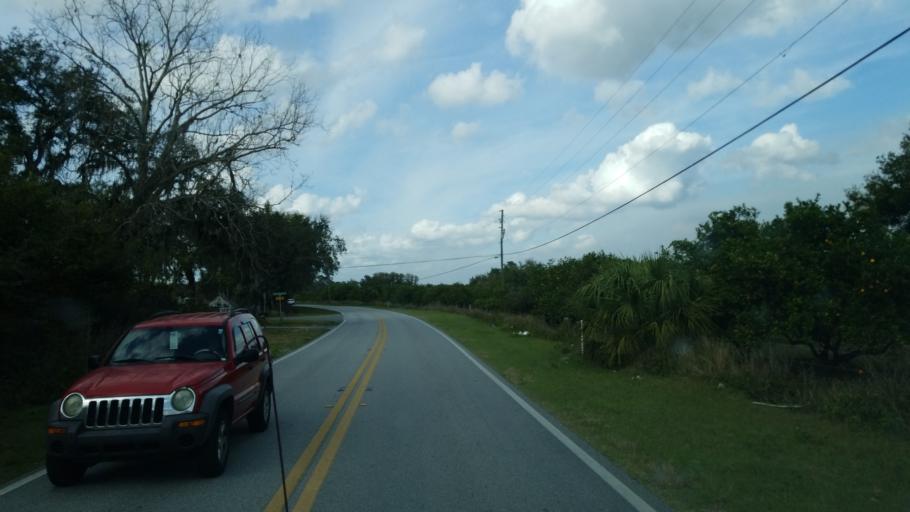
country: US
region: Florida
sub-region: Polk County
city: Davenport
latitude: 28.1969
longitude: -81.5945
